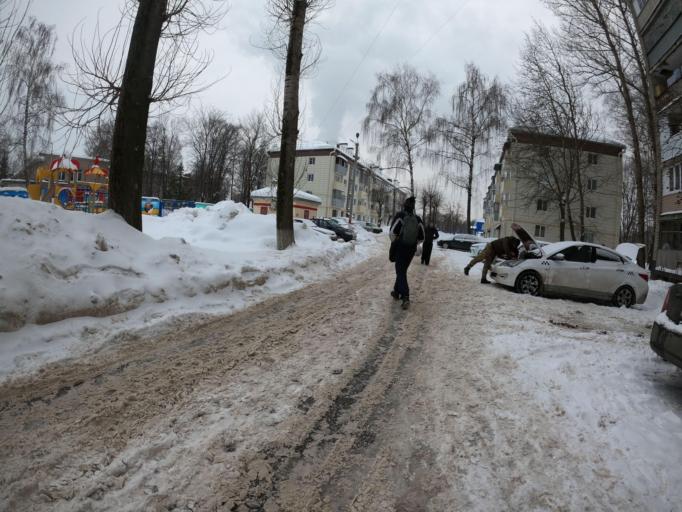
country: RU
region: Moskovskaya
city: Elektrogorsk
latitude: 55.8677
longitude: 38.7814
